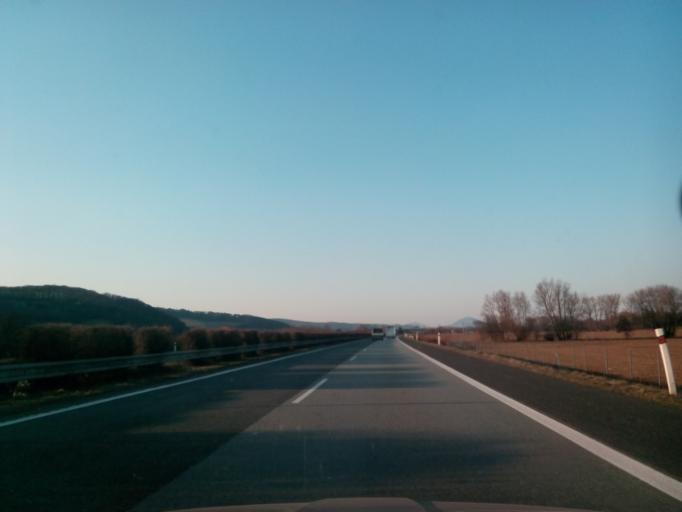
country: SK
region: Presovsky
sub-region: Okres Presov
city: Presov
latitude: 48.8870
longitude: 21.2495
